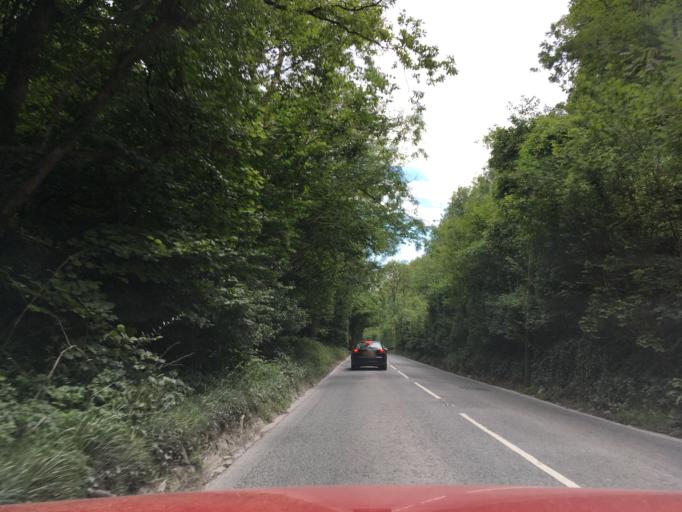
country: GB
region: England
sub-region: Somerset
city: Cheddar
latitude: 51.2977
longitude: -2.7899
